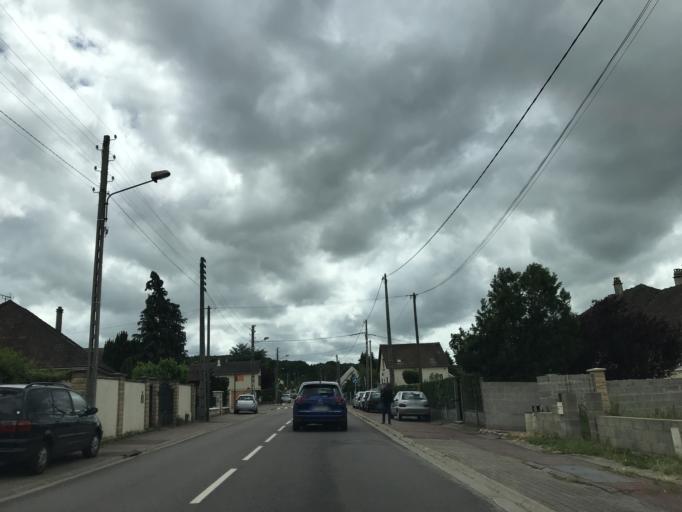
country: FR
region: Ile-de-France
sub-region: Departement des Yvelines
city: Rosny-sur-Seine
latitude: 48.9974
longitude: 1.6252
